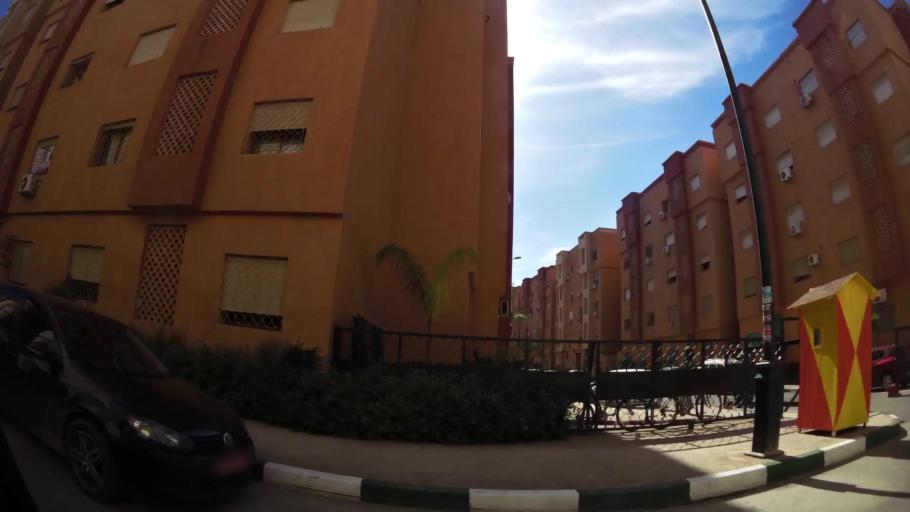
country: MA
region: Marrakech-Tensift-Al Haouz
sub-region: Marrakech
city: Marrakesh
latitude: 31.6604
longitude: -8.0208
